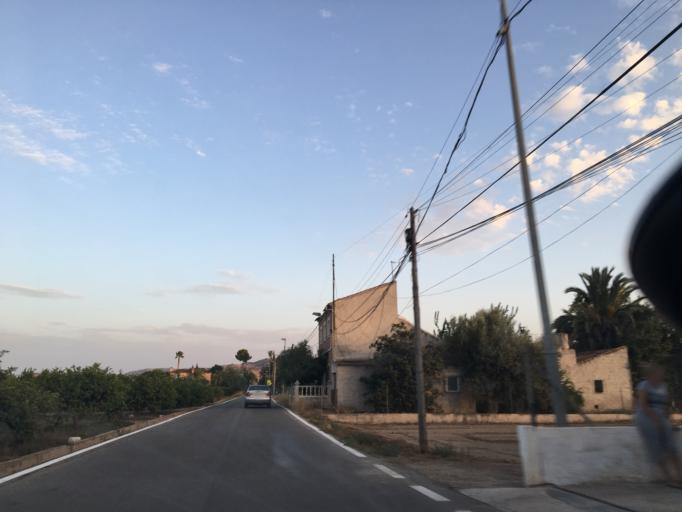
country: ES
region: Murcia
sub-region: Murcia
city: Santomera
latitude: 38.0271
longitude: -1.0573
